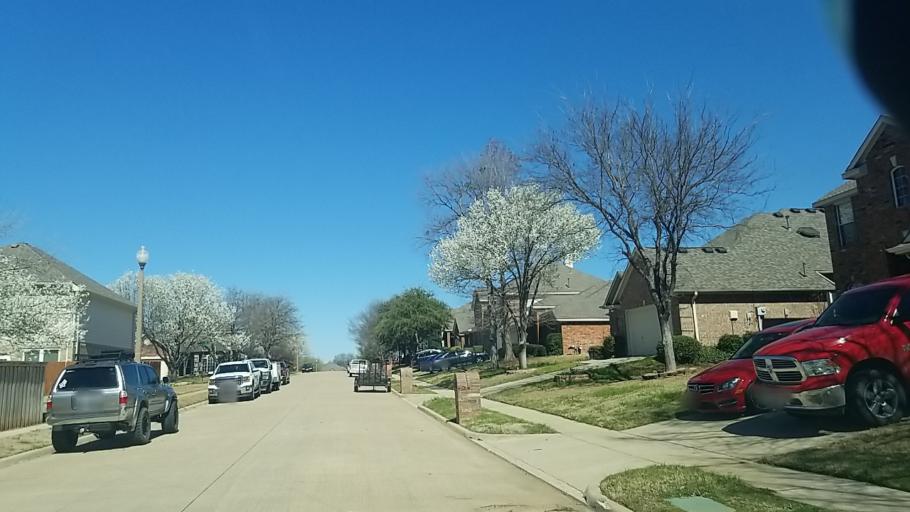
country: US
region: Texas
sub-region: Denton County
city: Corinth
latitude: 33.1598
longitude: -97.0894
